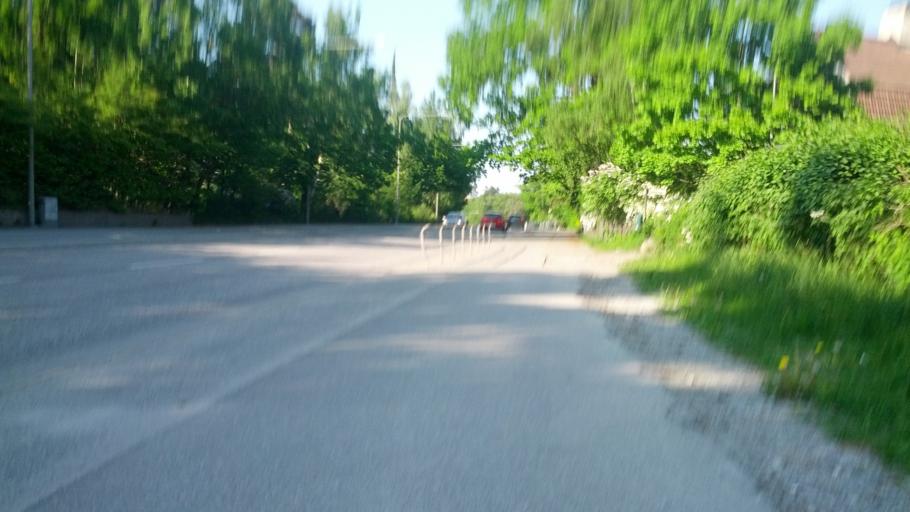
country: SE
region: Stockholm
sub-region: Danderyds Kommun
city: Djursholm
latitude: 59.3967
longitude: 18.0527
